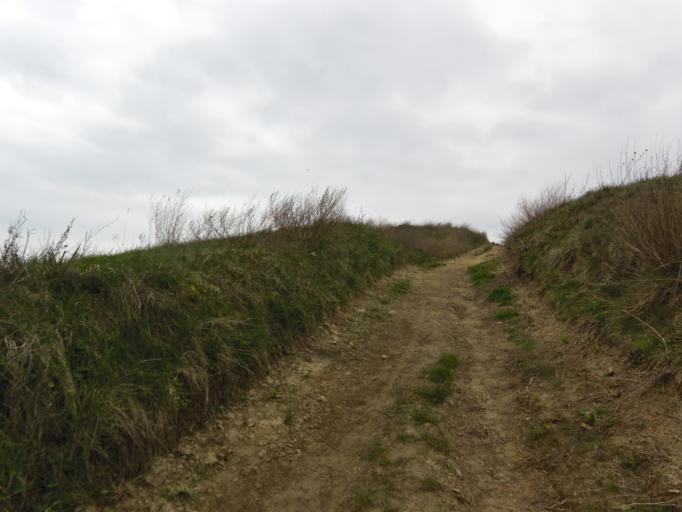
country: DE
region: Mecklenburg-Vorpommern
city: Hiddensee
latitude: 54.5924
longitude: 13.1254
